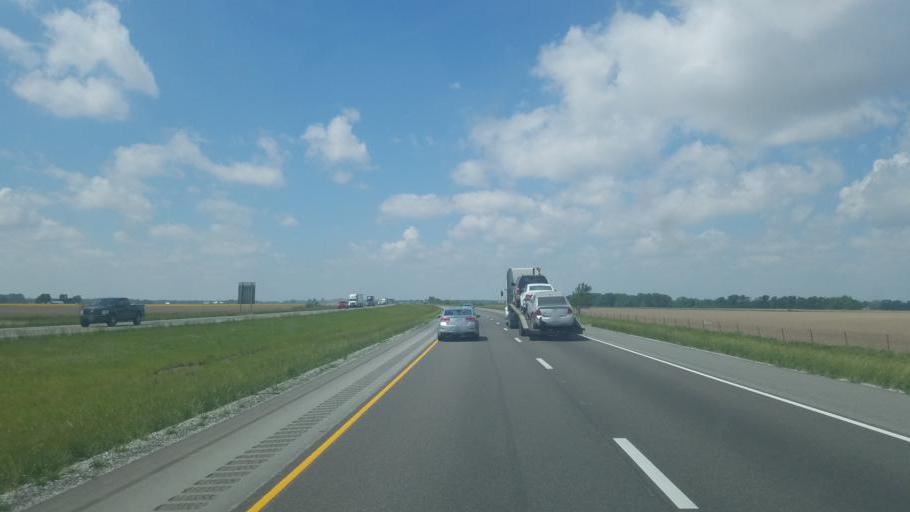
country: US
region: Illinois
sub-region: Clark County
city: Casey
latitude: 39.3144
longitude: -88.0046
